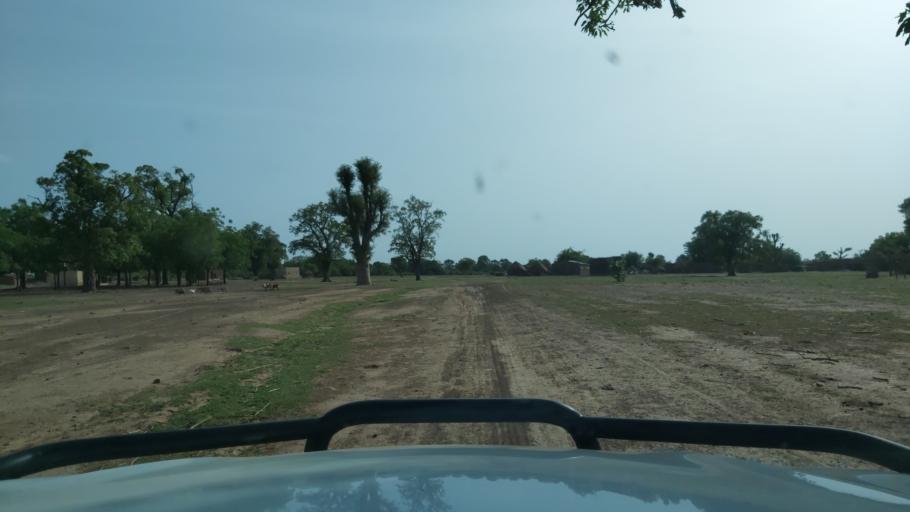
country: ML
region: Koulikoro
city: Koulikoro
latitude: 13.1651
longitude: -7.7931
